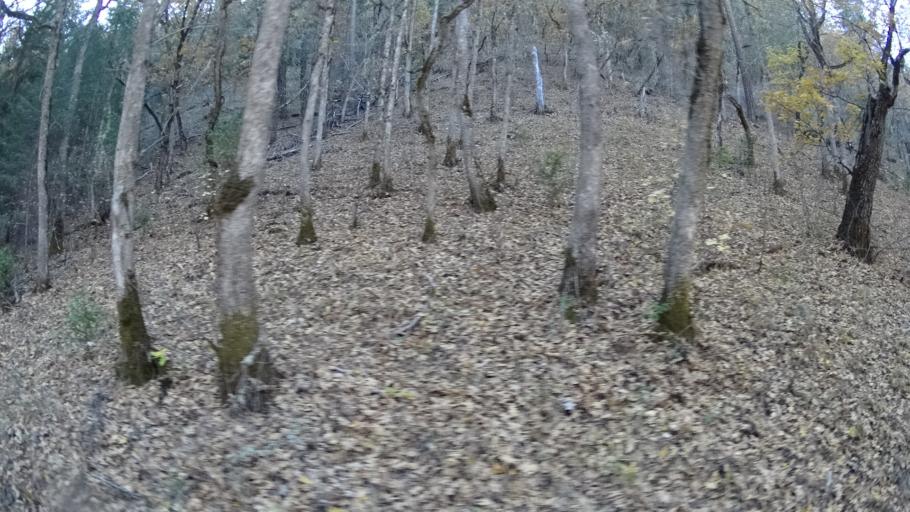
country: US
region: California
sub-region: Siskiyou County
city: Yreka
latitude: 41.8642
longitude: -122.7960
